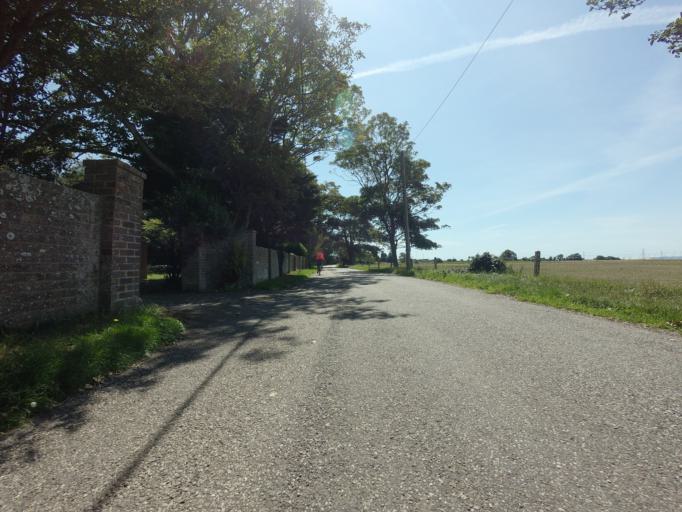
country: GB
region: England
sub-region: Kent
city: Lydd
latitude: 50.9570
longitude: 0.9038
